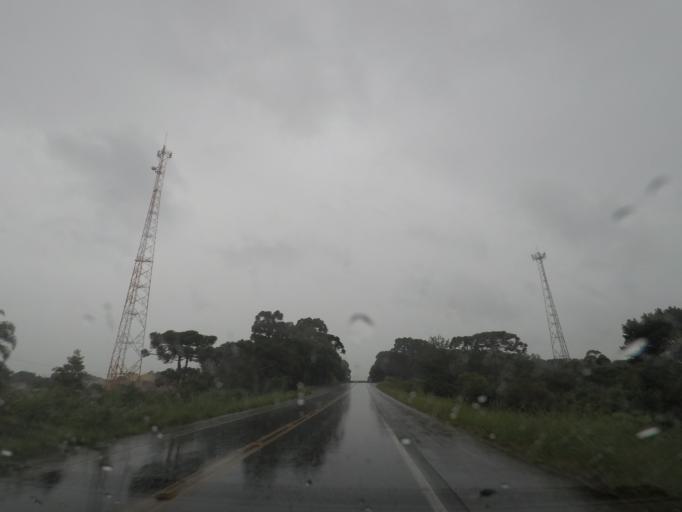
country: BR
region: Parana
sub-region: Almirante Tamandare
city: Almirante Tamandare
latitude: -25.3537
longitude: -49.2955
